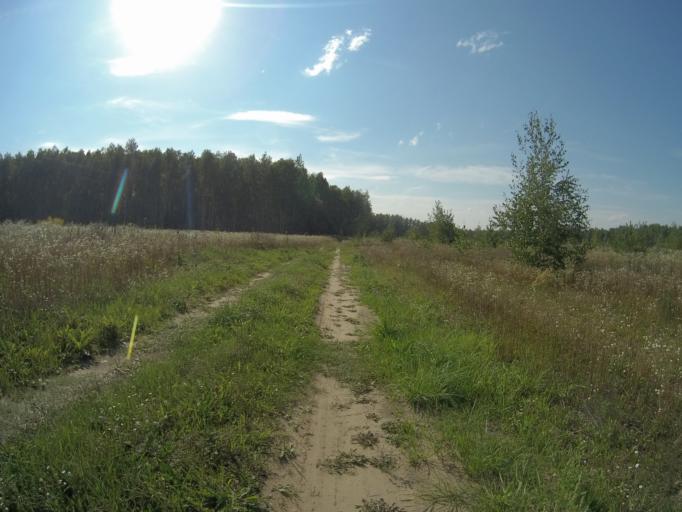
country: RU
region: Vladimir
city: Raduzhnyy
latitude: 55.9883
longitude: 40.2438
